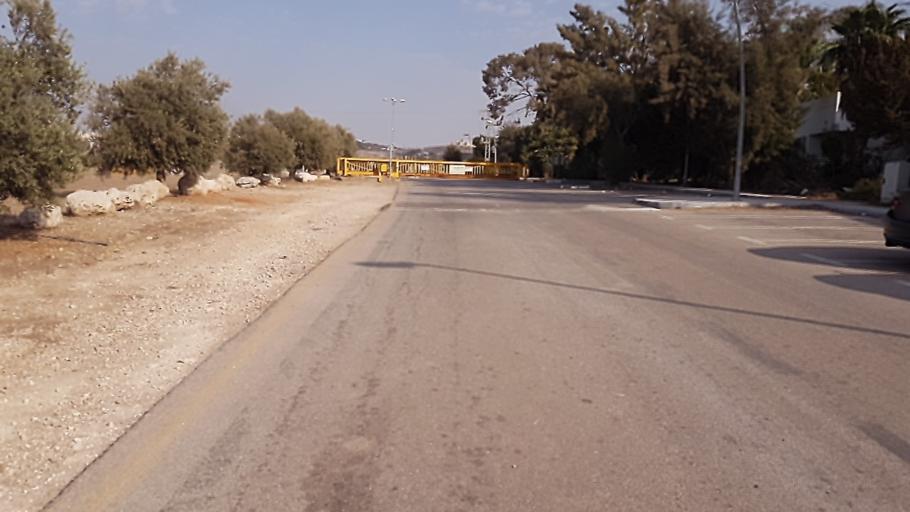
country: IL
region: Central District
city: Rosh Ha'Ayin
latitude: 32.0852
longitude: 34.9403
